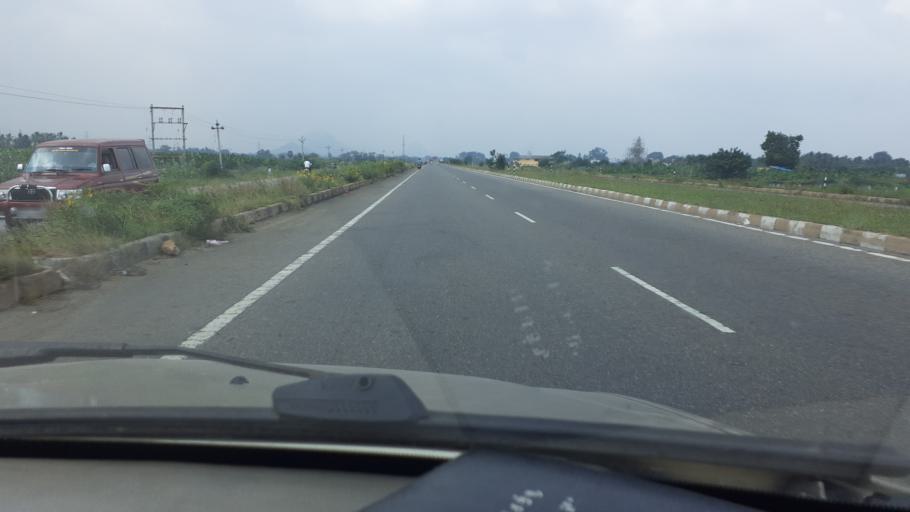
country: IN
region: Tamil Nadu
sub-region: Tirunelveli Kattabo
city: Nanguneri
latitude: 8.4834
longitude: 77.6601
